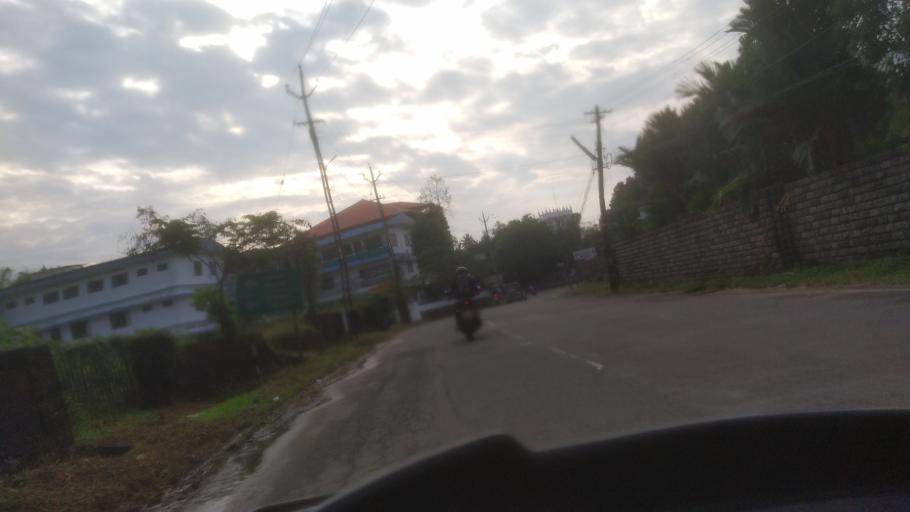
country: IN
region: Kerala
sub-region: Ernakulam
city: Kotamangalam
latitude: 10.0671
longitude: 76.6264
